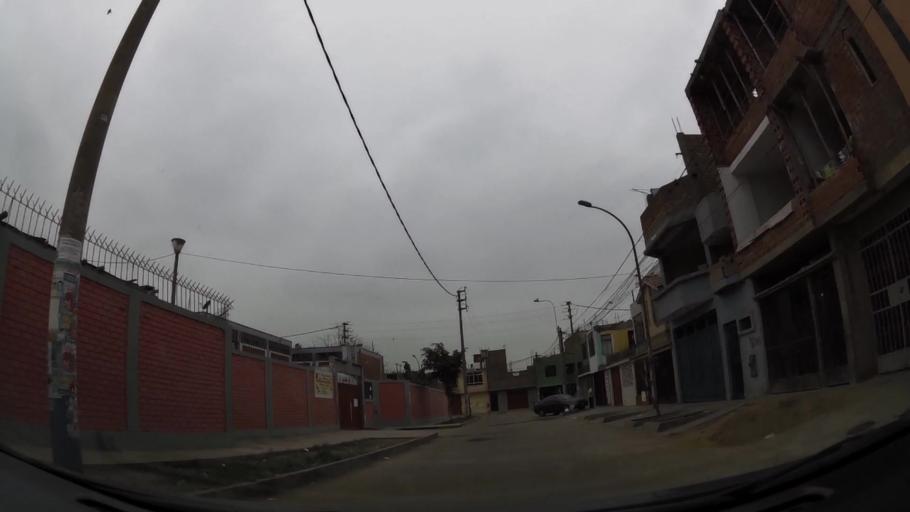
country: PE
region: Lima
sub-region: Lima
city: Independencia
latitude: -11.9636
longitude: -77.0614
